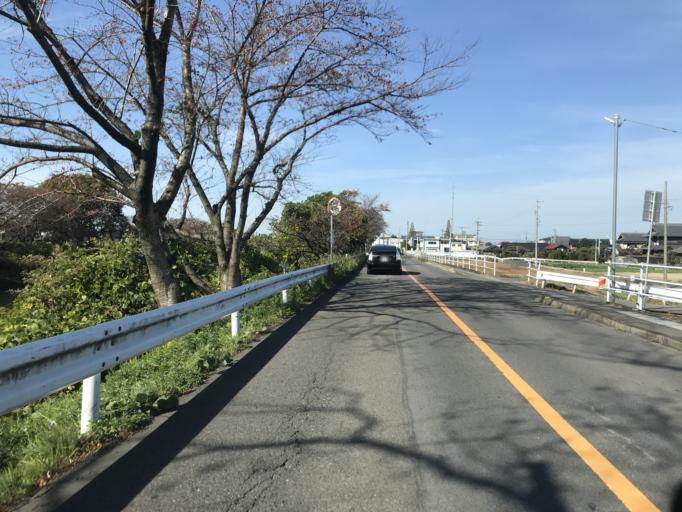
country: JP
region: Aichi
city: Iwakura
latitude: 35.2326
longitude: 136.8444
